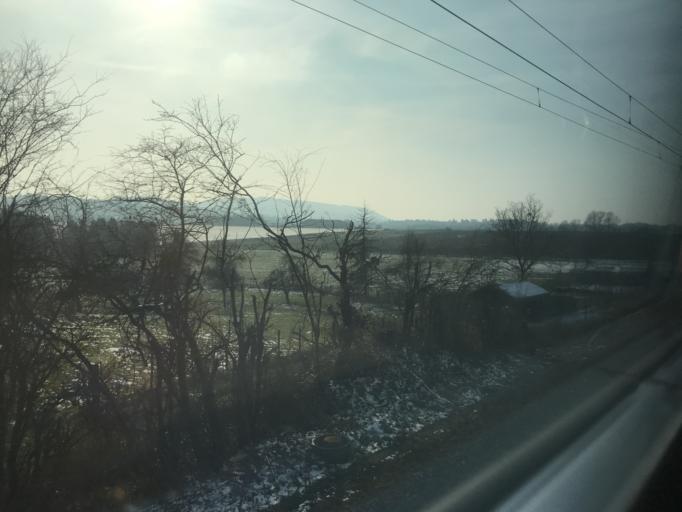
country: DE
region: Rheinland-Pfalz
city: Urzig
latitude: 49.9919
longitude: 6.9973
